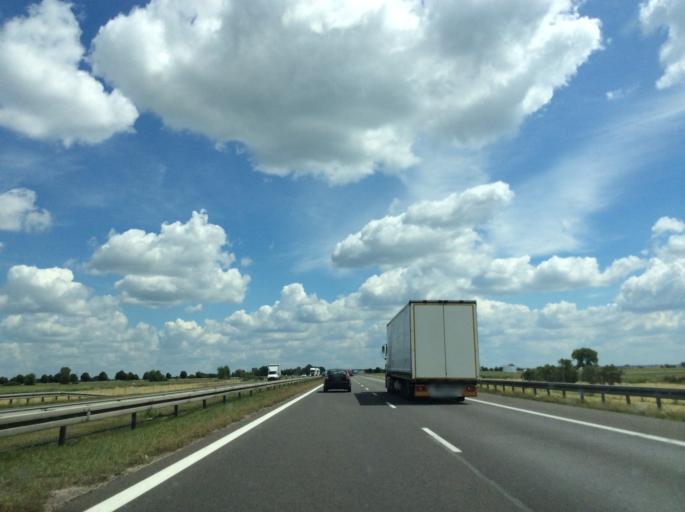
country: PL
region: Greater Poland Voivodeship
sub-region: Powiat slupecki
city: Ladek
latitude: 52.2104
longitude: 17.9961
